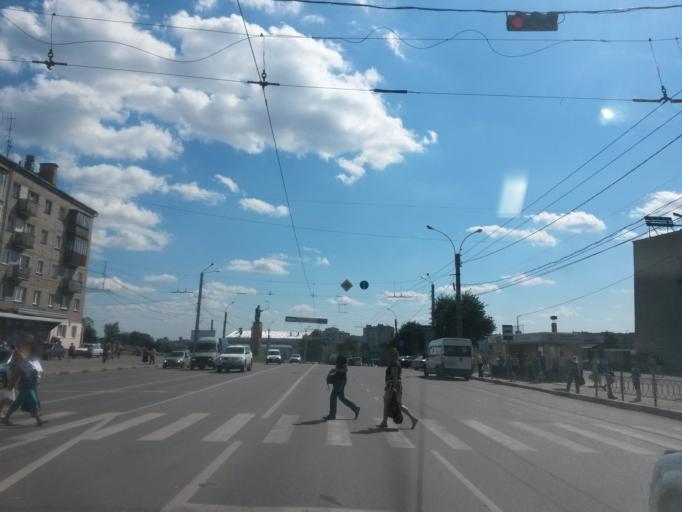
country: RU
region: Ivanovo
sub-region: Gorod Ivanovo
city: Ivanovo
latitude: 57.0082
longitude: 40.9899
